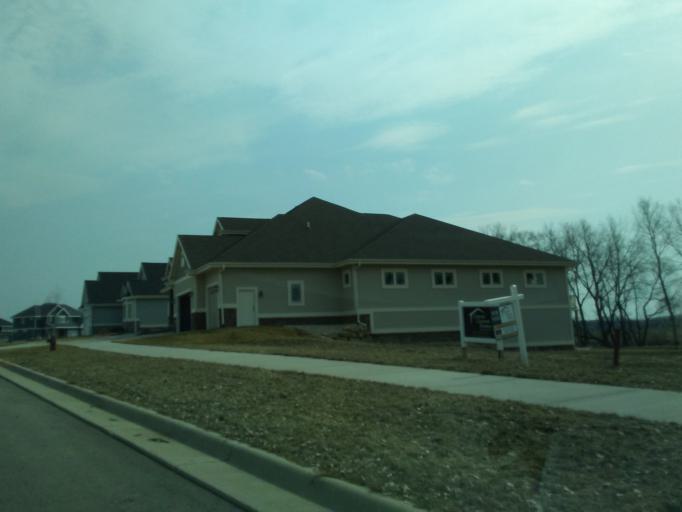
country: US
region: Wisconsin
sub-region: Dane County
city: Waunakee
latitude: 43.1694
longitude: -89.4559
